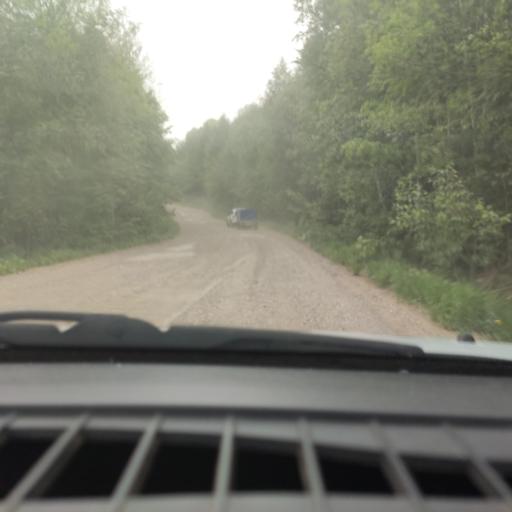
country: RU
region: Perm
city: Novyye Lyady
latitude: 57.8986
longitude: 56.6555
